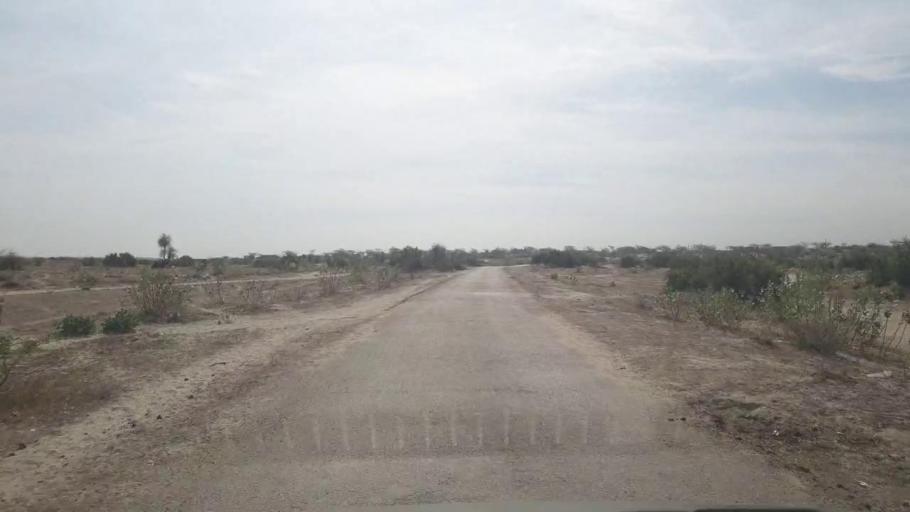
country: PK
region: Sindh
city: Umarkot
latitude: 25.2824
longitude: 69.7442
